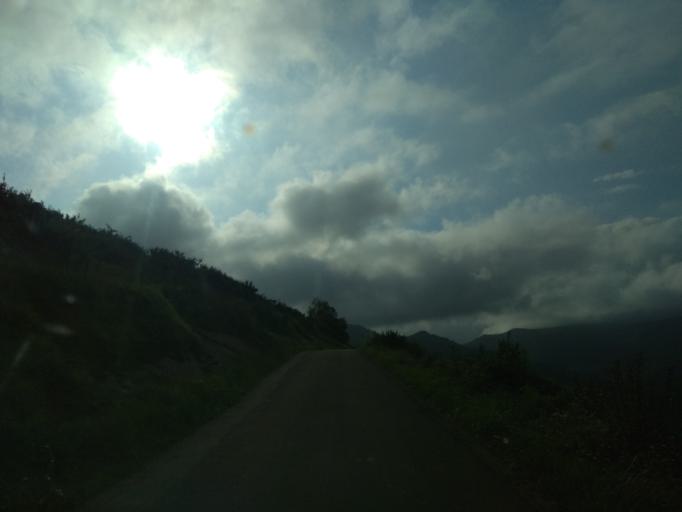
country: ES
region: Cantabria
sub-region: Provincia de Cantabria
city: San Vicente de la Barquera
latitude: 43.3118
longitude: -4.3854
